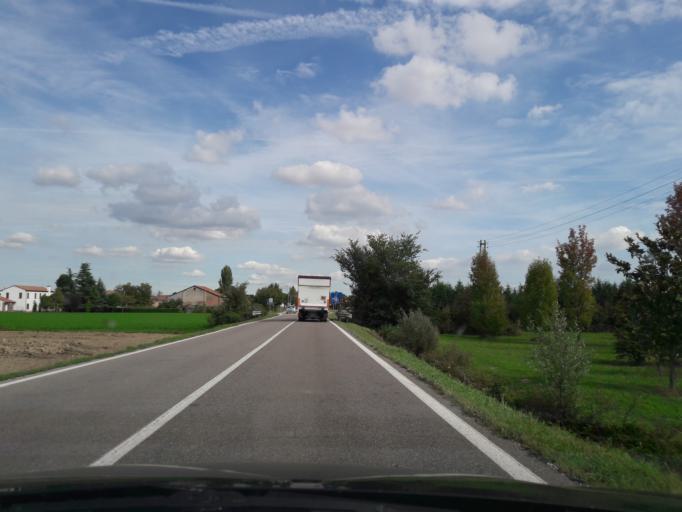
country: IT
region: Veneto
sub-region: Provincia di Rovigo
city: Villanova del Ghebbo Canton
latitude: 45.0756
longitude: 11.6519
